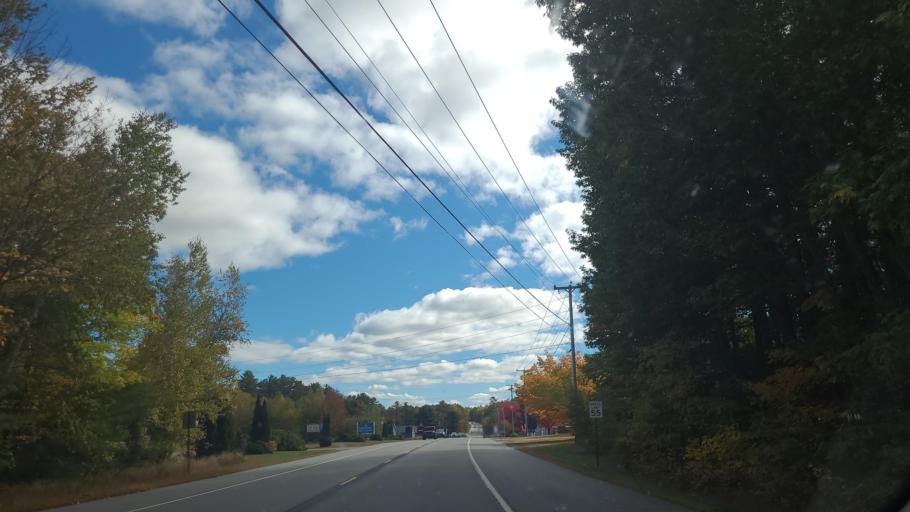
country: US
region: Maine
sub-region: Cumberland County
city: Raymond
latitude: 43.9130
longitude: -70.5145
